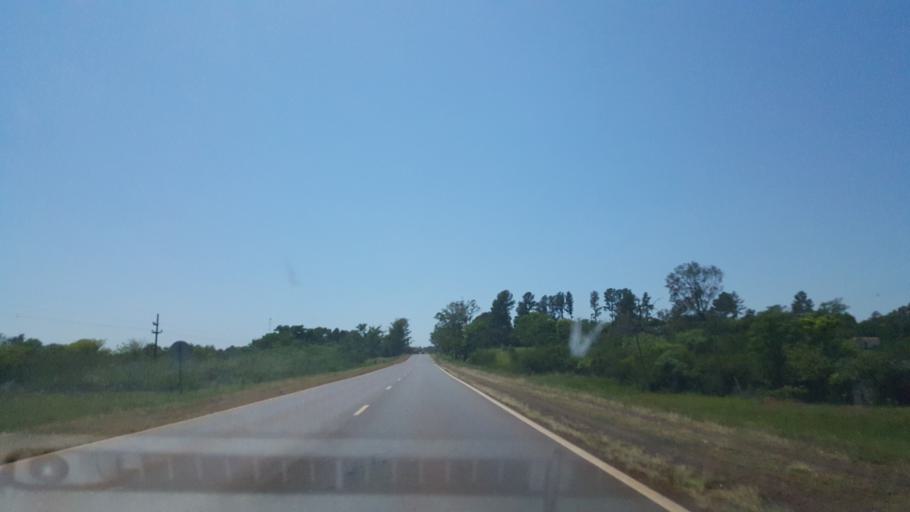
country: AR
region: Corrientes
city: Santo Tome
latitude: -28.5459
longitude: -56.0850
